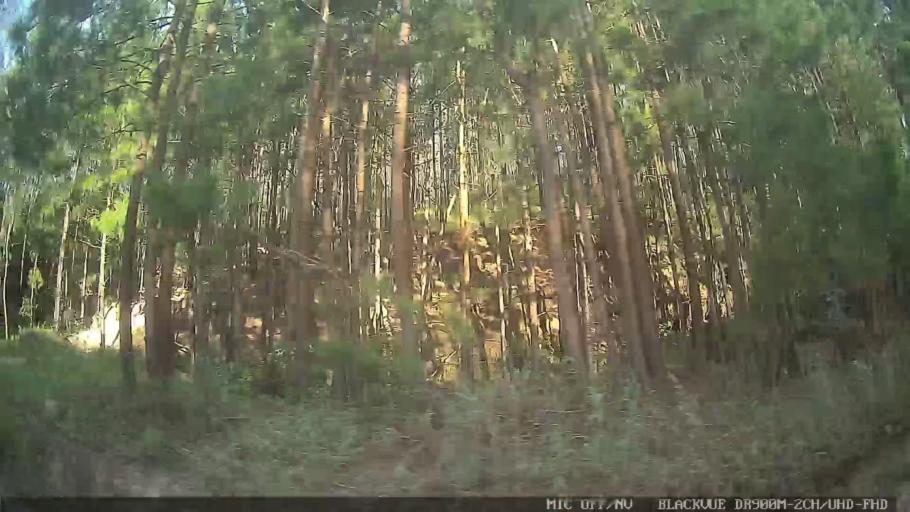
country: BR
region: Sao Paulo
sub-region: Bom Jesus Dos Perdoes
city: Bom Jesus dos Perdoes
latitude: -23.1604
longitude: -46.5148
